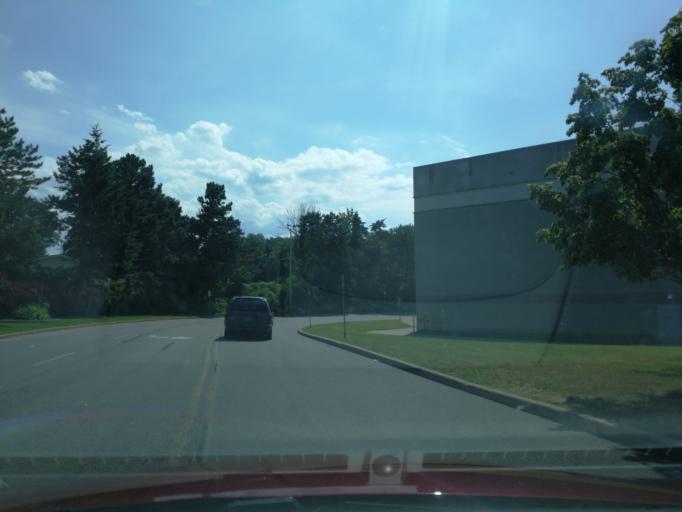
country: US
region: New York
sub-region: Monroe County
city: Greece
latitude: 43.2050
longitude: -77.6877
